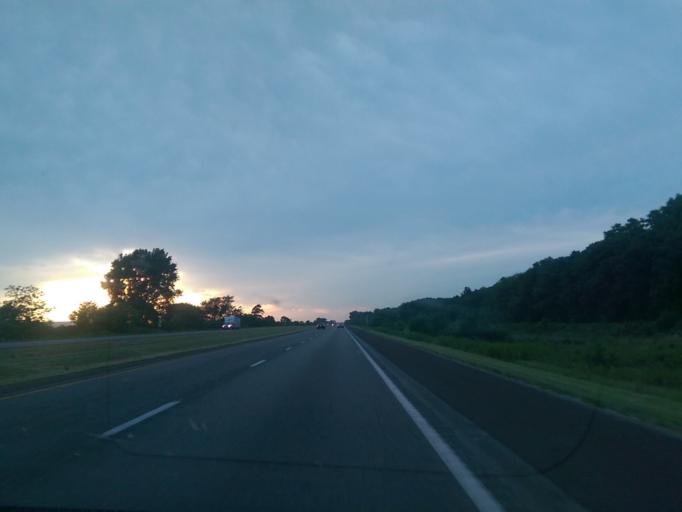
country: US
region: Missouri
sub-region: Holt County
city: Mound City
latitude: 40.2178
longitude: -95.3879
